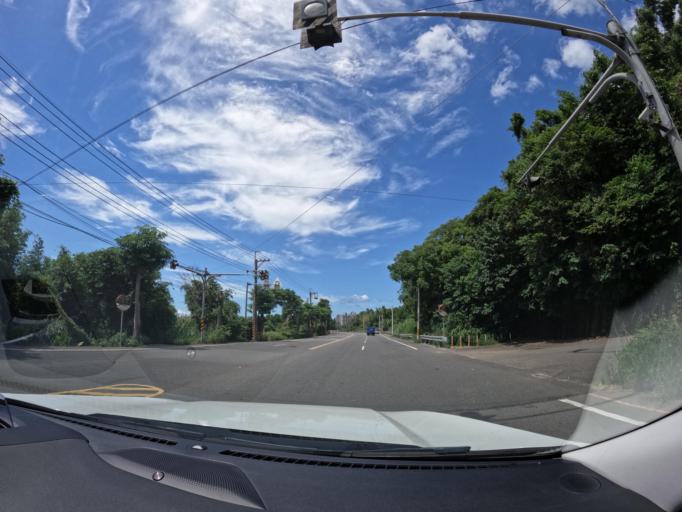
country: TW
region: Taipei
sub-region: Taipei
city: Banqiao
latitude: 25.1342
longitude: 121.3921
